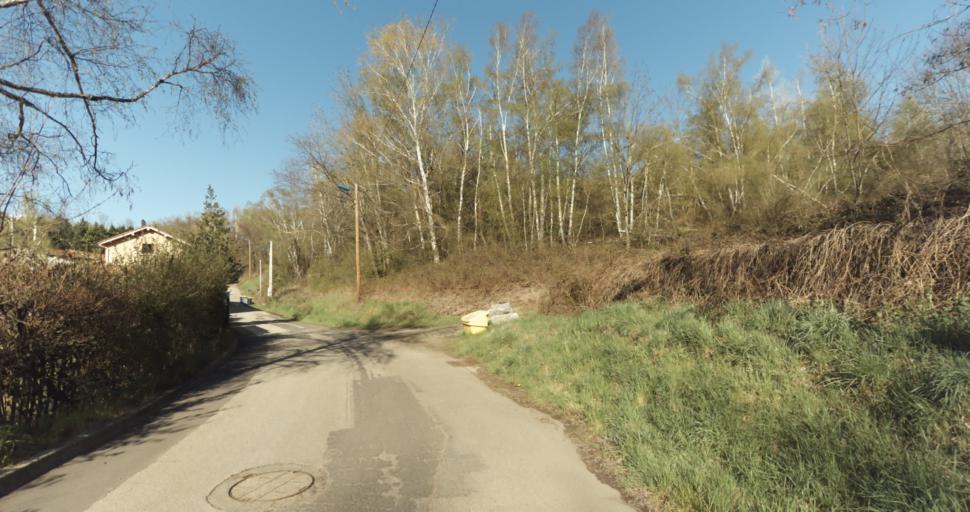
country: FR
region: Rhone-Alpes
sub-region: Departement de la Loire
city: La Talaudiere
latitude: 45.4690
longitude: 4.4404
